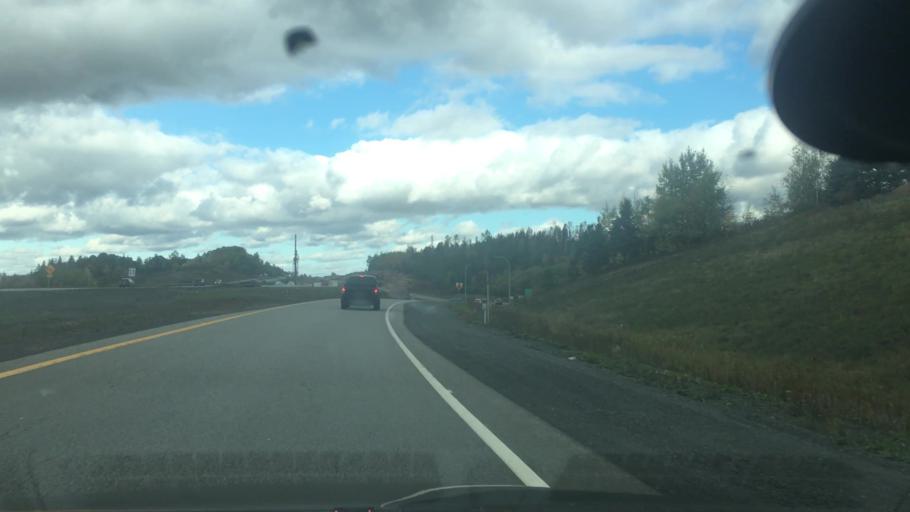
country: CA
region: Nova Scotia
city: Windsor
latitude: 44.9713
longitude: -64.0963
